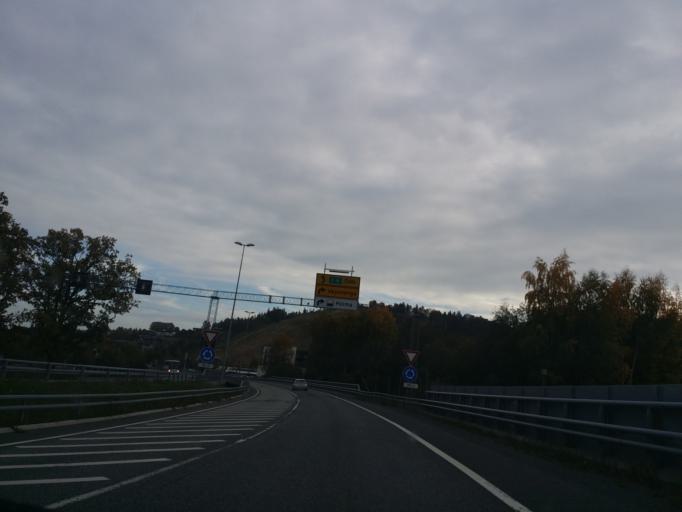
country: NO
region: Akershus
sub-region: Baerum
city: Skui
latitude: 59.9118
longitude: 10.4773
